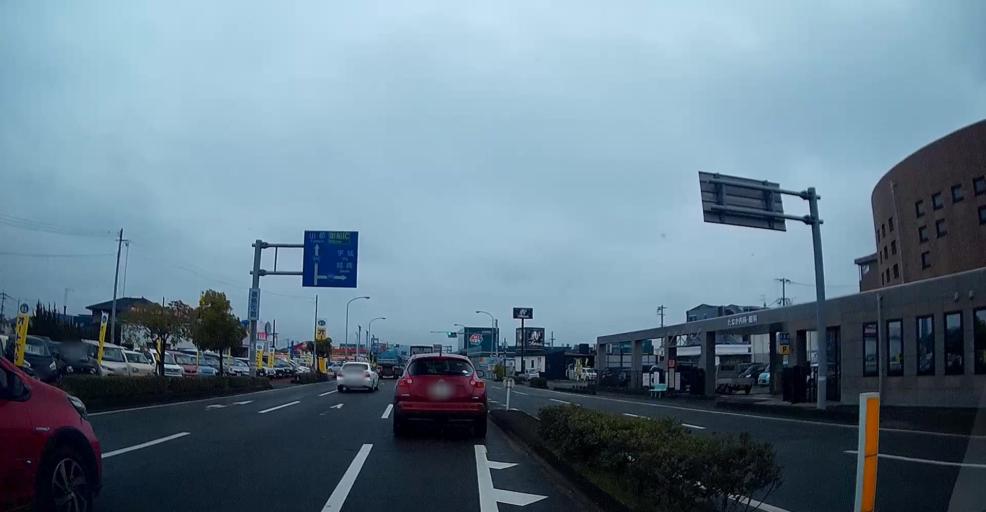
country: JP
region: Kumamoto
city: Kumamoto
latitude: 32.7497
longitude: 130.7394
